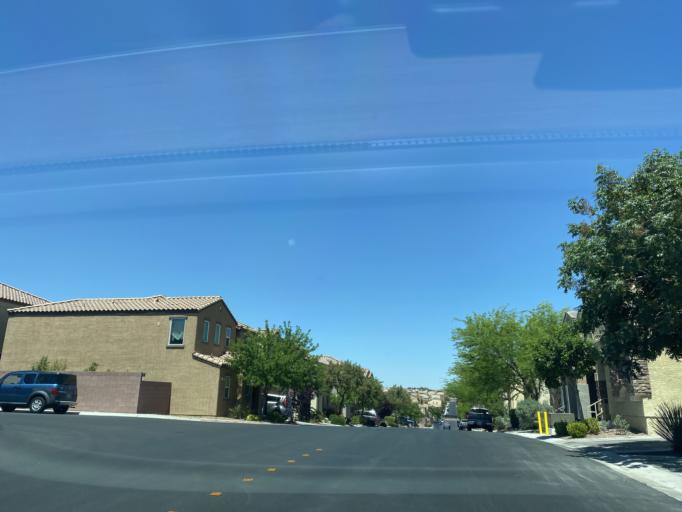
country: US
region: Nevada
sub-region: Clark County
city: Summerlin South
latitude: 36.2256
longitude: -115.3264
